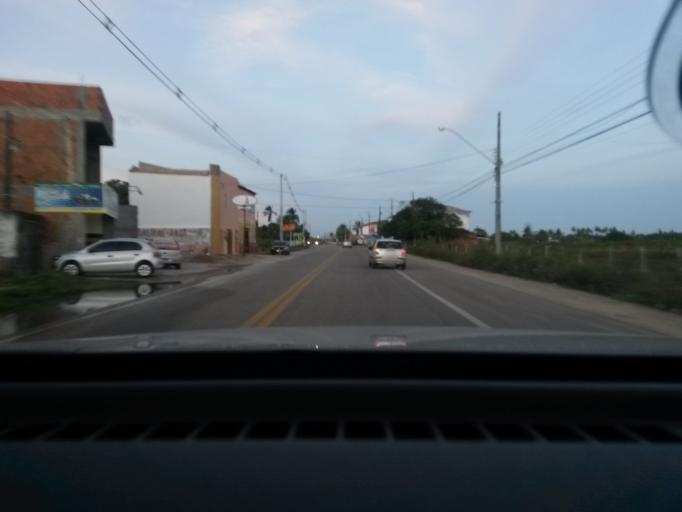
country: BR
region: Sergipe
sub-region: Sao Cristovao
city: Sao Cristovao
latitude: -11.0893
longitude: -37.1346
